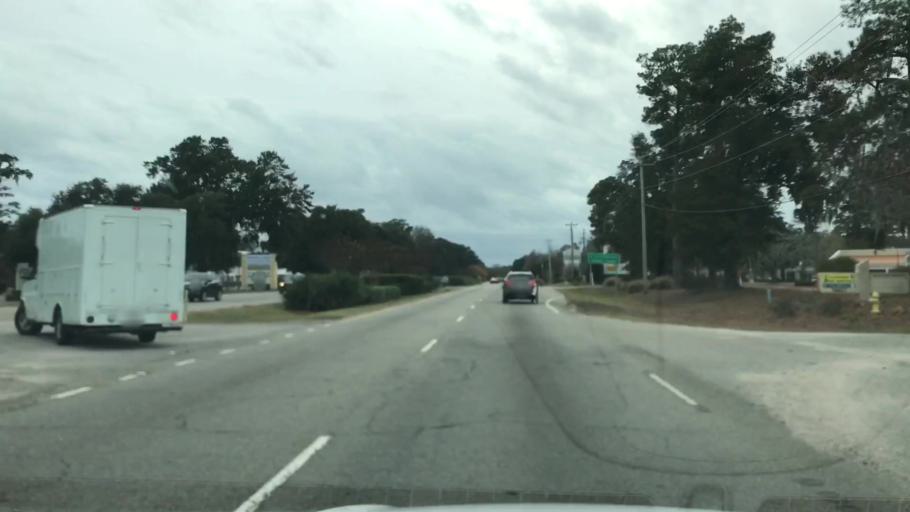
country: US
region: South Carolina
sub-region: Georgetown County
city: Murrells Inlet
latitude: 33.4890
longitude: -79.0922
